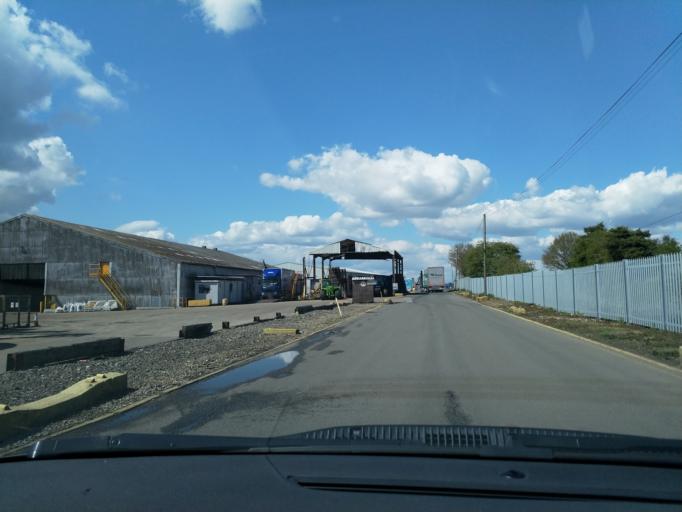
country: GB
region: England
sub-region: Oxfordshire
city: Adderbury
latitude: 52.0347
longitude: -1.2921
